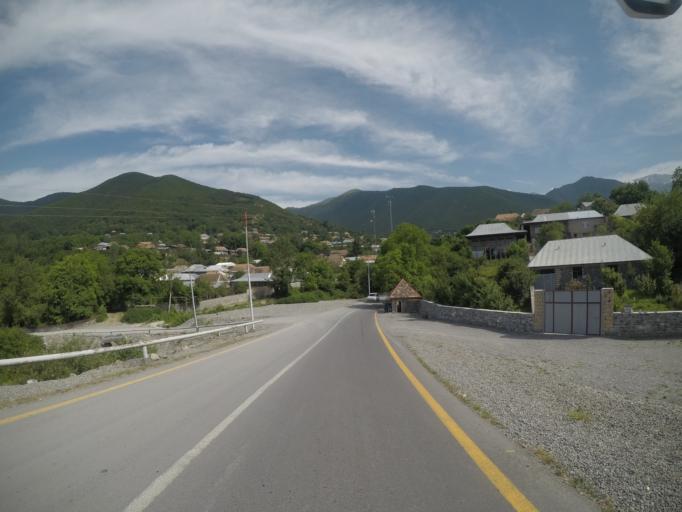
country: AZ
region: Shaki City
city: Sheki
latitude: 41.2461
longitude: 47.1886
